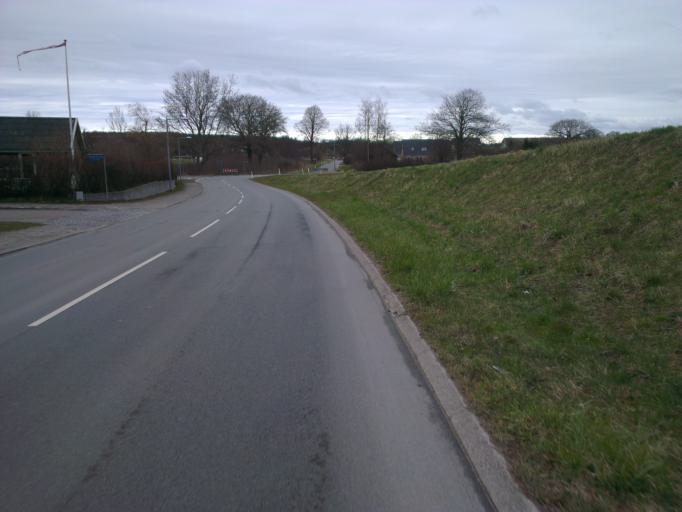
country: DK
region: Capital Region
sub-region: Frederikssund Kommune
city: Frederikssund
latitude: 55.8282
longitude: 12.0879
